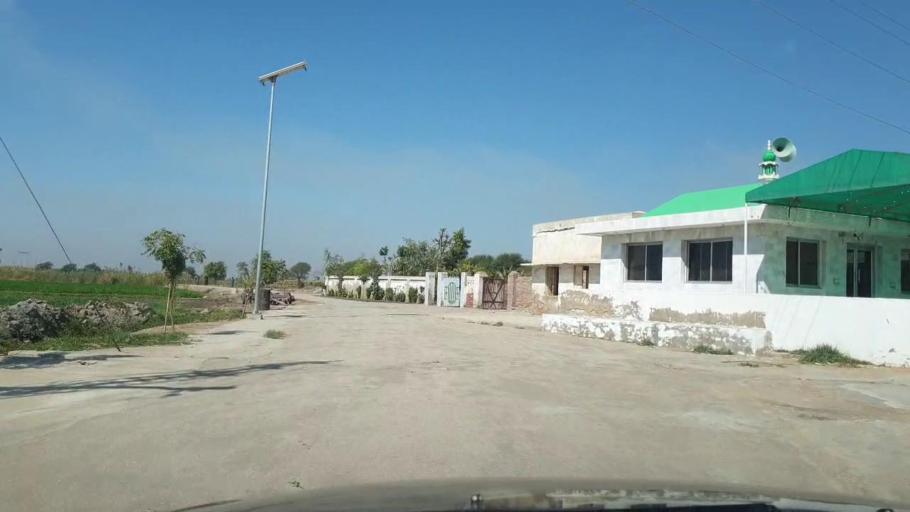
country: PK
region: Sindh
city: Mirpur Khas
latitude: 25.5643
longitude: 69.0580
